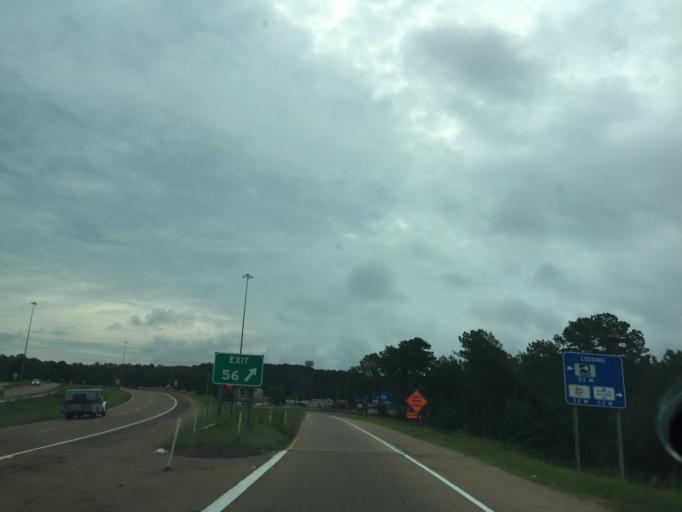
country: US
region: Mississippi
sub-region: Rankin County
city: Brandon
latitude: 32.2780
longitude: -90.0042
